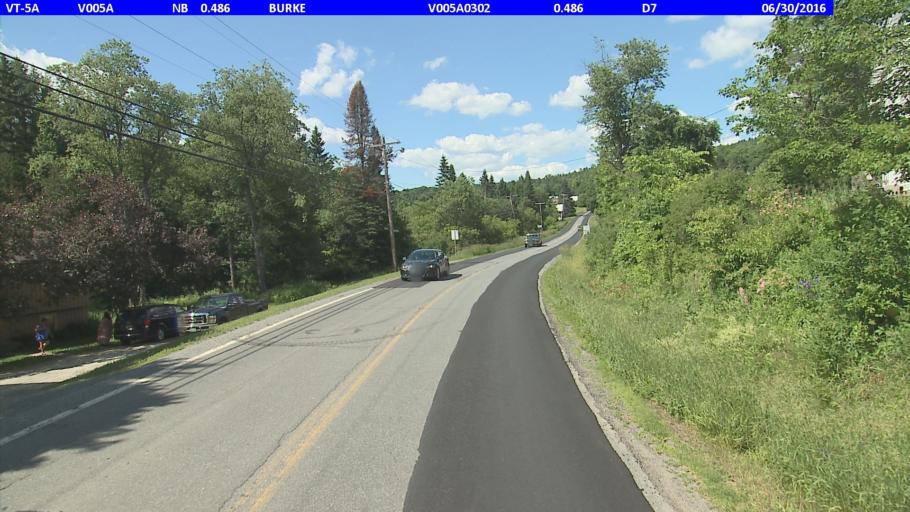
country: US
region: Vermont
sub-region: Caledonia County
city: Lyndonville
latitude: 44.6482
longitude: -71.9824
